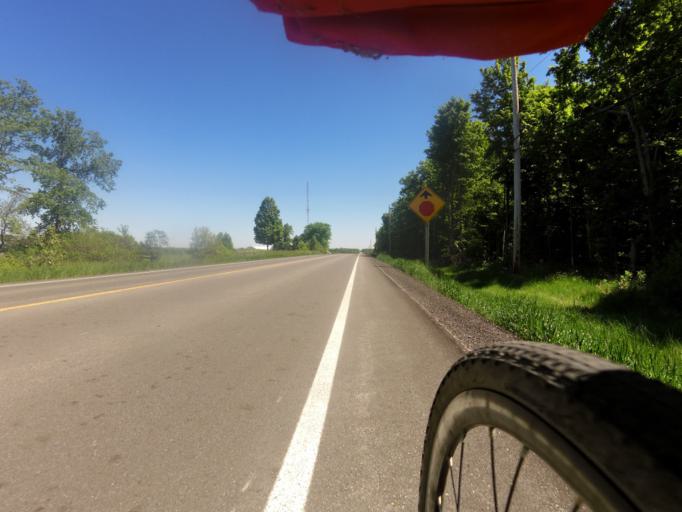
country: CA
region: Ontario
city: Carleton Place
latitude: 45.1637
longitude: -76.2956
